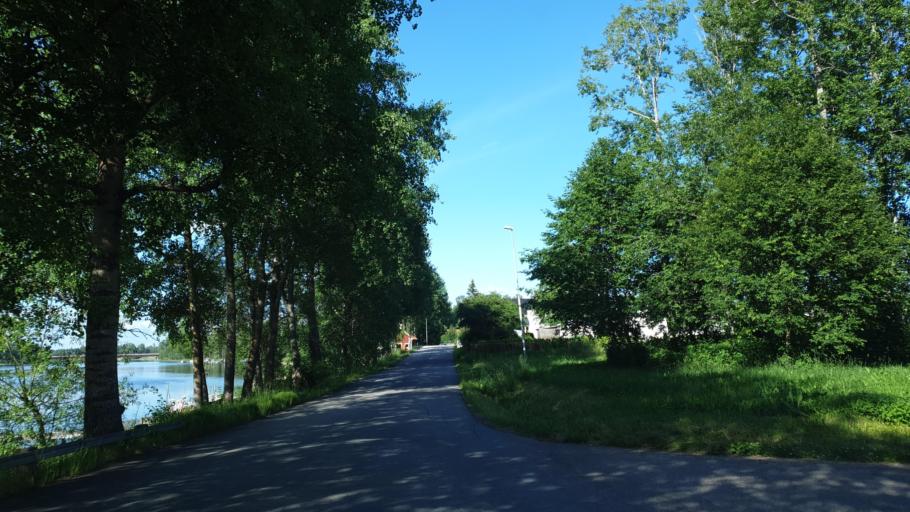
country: SE
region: Dalarna
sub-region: Avesta Kommun
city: Avesta
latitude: 60.1269
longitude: 16.2539
